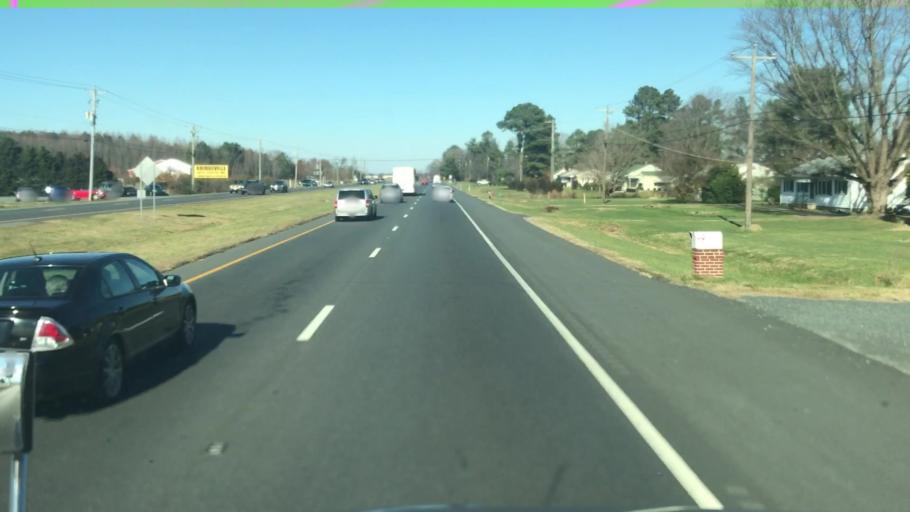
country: US
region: Delaware
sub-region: Sussex County
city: Bridgeville
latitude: 38.7021
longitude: -75.5887
